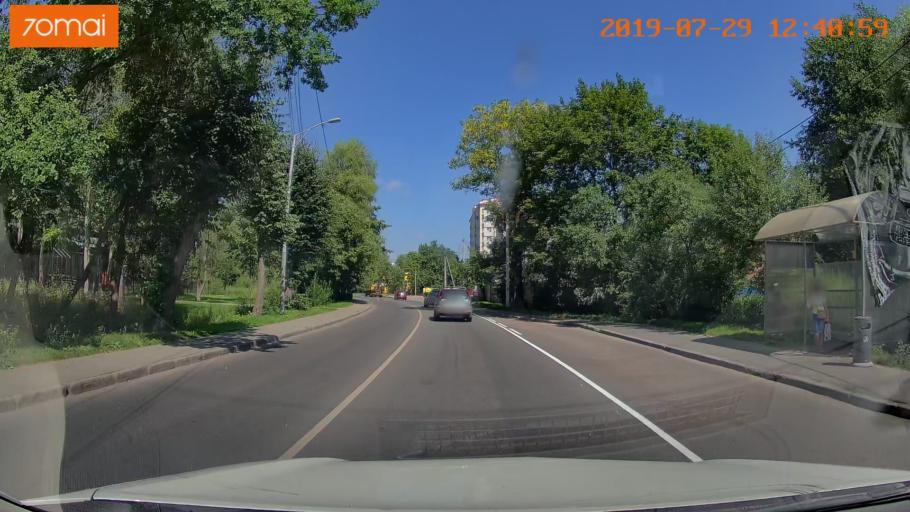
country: RU
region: Kaliningrad
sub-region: Gorod Kaliningrad
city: Kaliningrad
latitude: 54.6701
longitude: 20.5456
